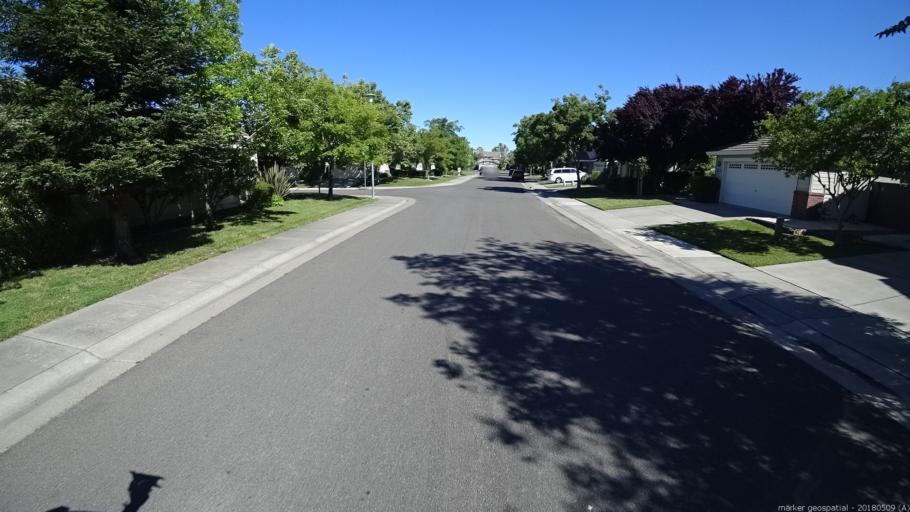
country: US
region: California
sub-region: Sacramento County
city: Elverta
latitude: 38.6695
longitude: -121.5230
